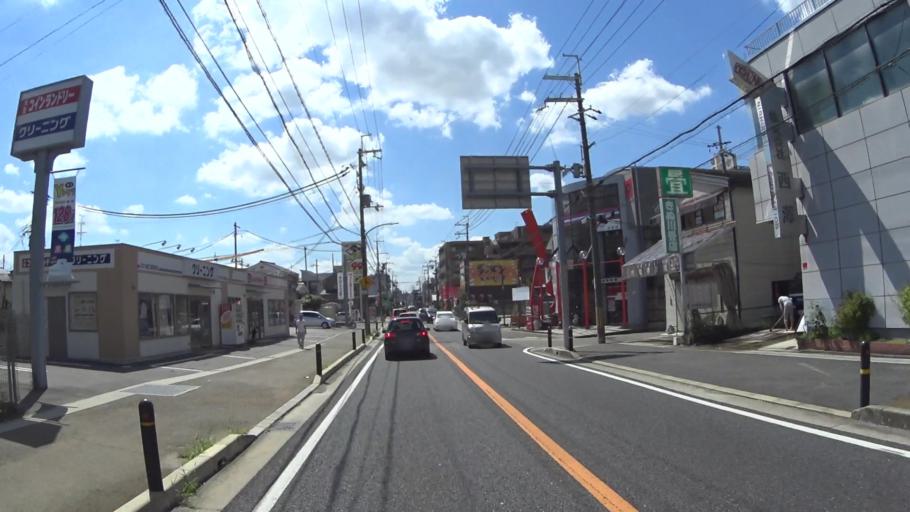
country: JP
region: Kyoto
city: Uji
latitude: 34.8848
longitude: 135.7807
